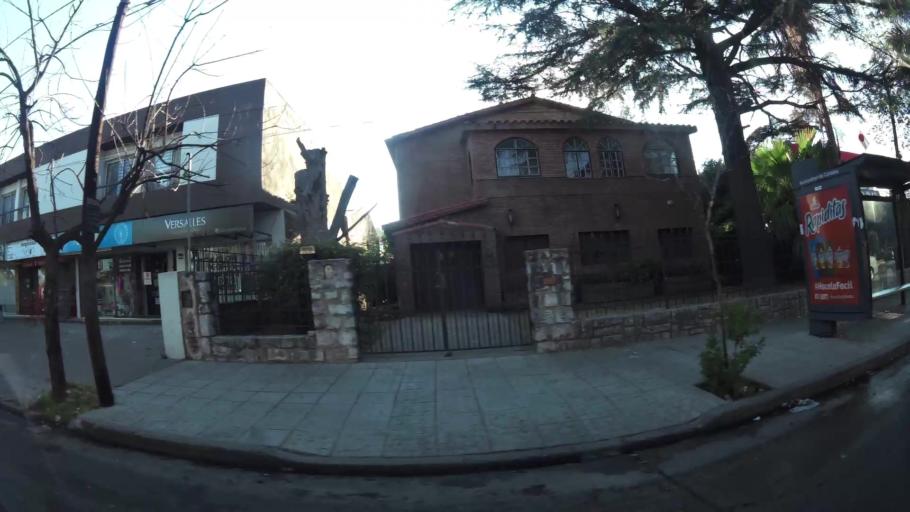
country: AR
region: Cordoba
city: Villa Allende
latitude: -31.3504
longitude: -64.2480
